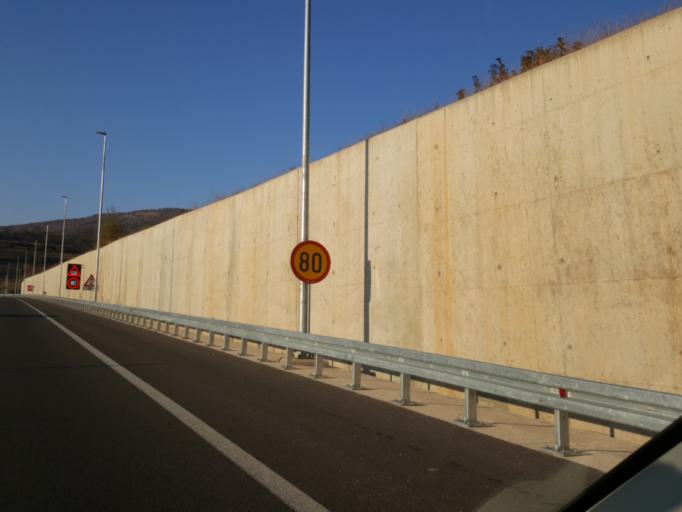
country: RS
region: Central Serbia
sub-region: Pirotski Okrug
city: Dimitrovgrad
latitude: 43.0209
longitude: 22.7965
